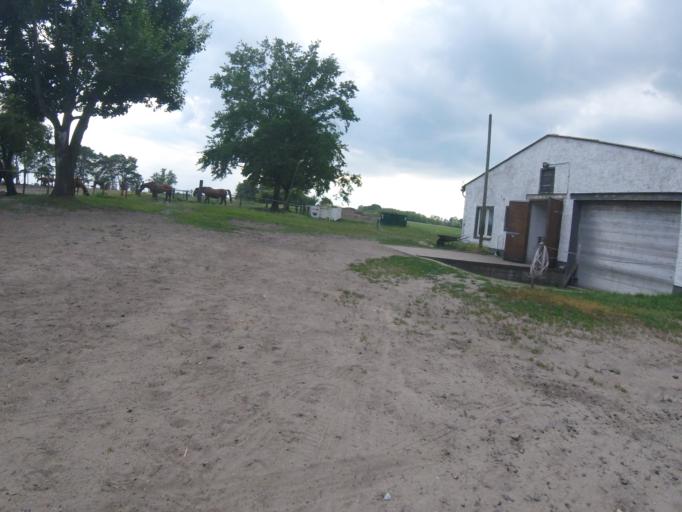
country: DE
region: Brandenburg
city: Konigs Wusterhausen
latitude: 52.2743
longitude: 13.5958
